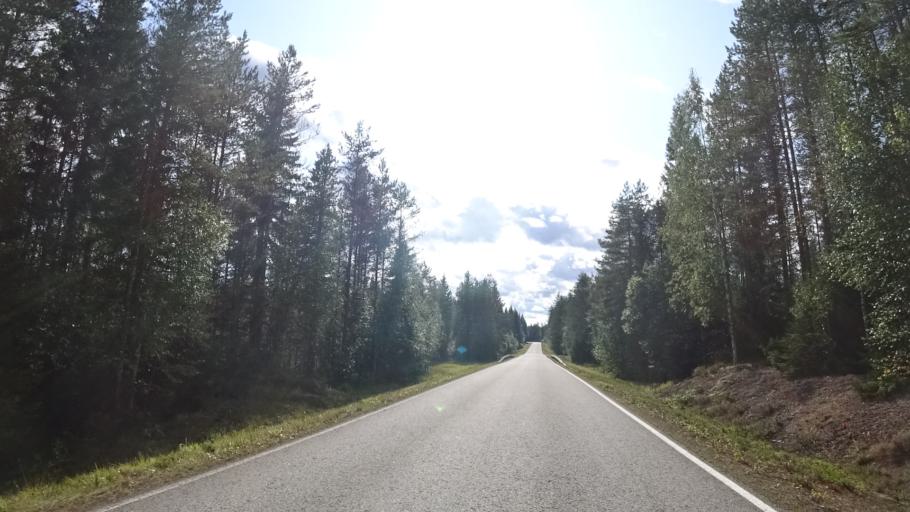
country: RU
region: Republic of Karelia
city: Vyartsilya
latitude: 62.2456
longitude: 30.7158
